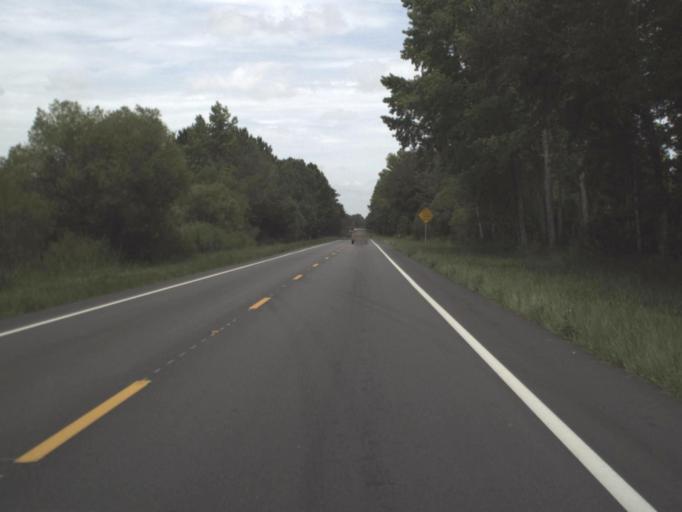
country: US
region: Florida
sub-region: Jefferson County
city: Monticello
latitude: 30.4831
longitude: -83.6874
